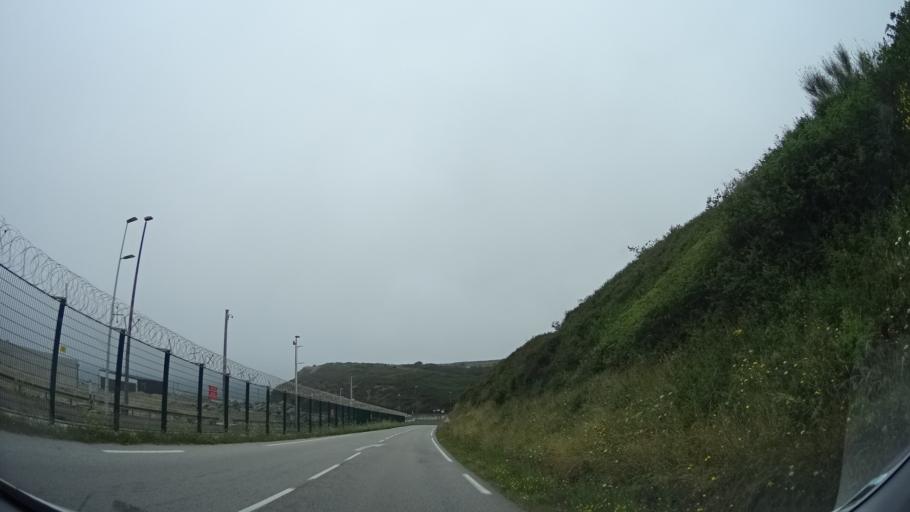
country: FR
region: Lower Normandy
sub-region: Departement de la Manche
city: Flamanville
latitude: 49.5412
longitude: -1.8739
